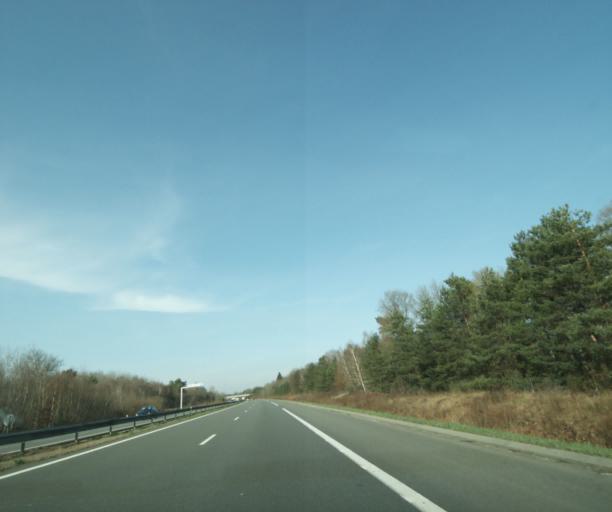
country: FR
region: Centre
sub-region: Departement du Loir-et-Cher
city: Salbris
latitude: 47.4723
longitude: 2.0086
